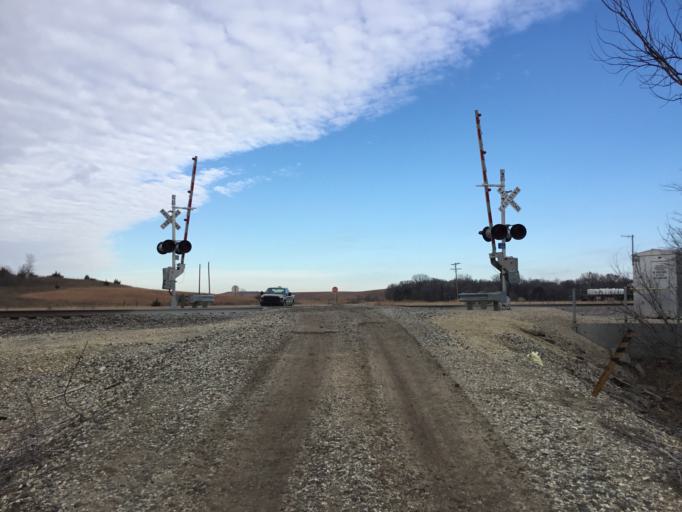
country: US
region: Kansas
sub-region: Chase County
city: Cottonwood Falls
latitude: 38.2836
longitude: -96.7689
